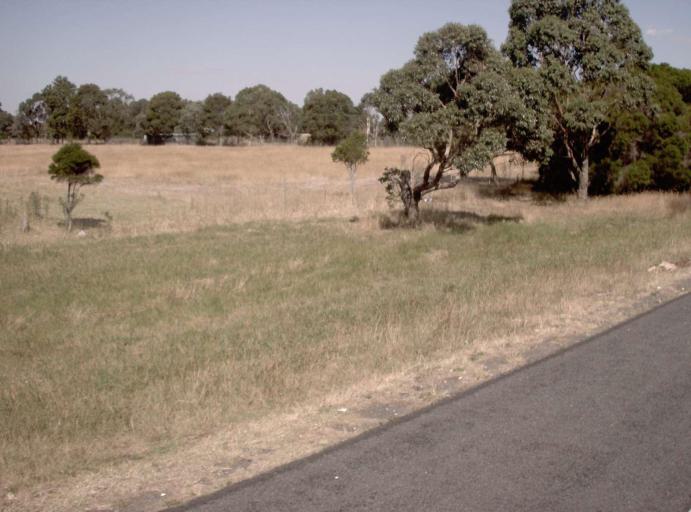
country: AU
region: Victoria
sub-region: Kingston
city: Chelsea Heights
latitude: -38.0288
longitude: 145.1364
